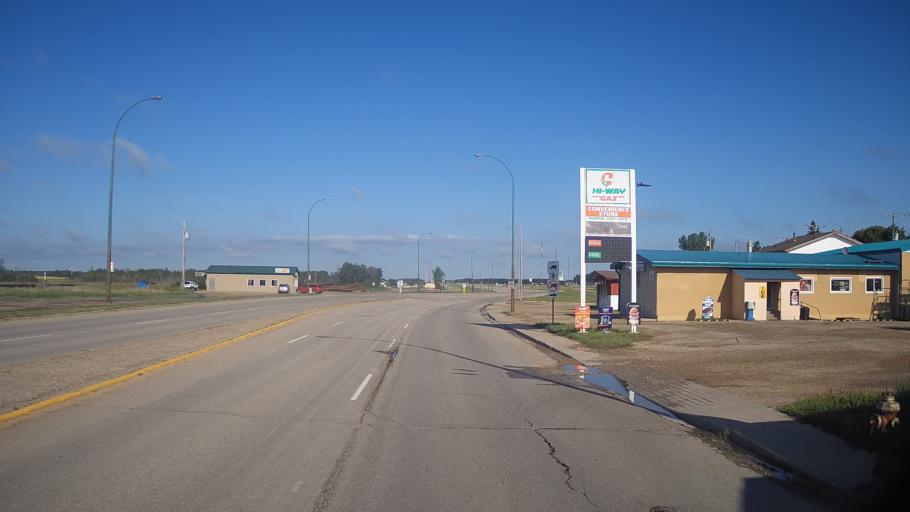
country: CA
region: Saskatchewan
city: Lanigan
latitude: 51.8459
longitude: -105.0365
